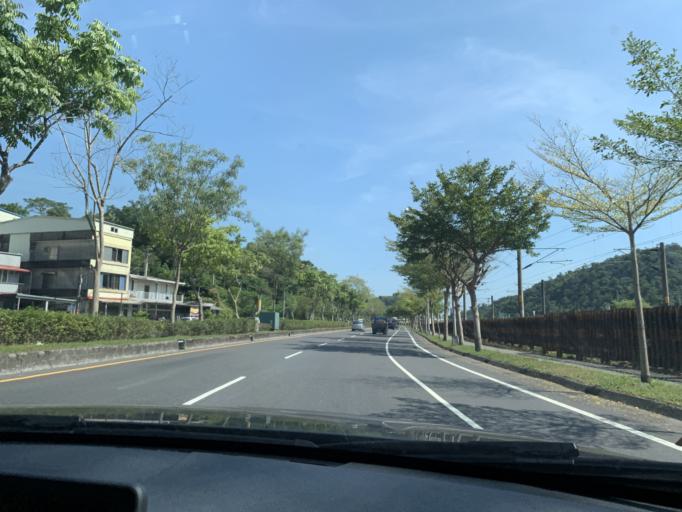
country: TW
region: Taiwan
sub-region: Yilan
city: Yilan
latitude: 24.5991
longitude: 121.8343
